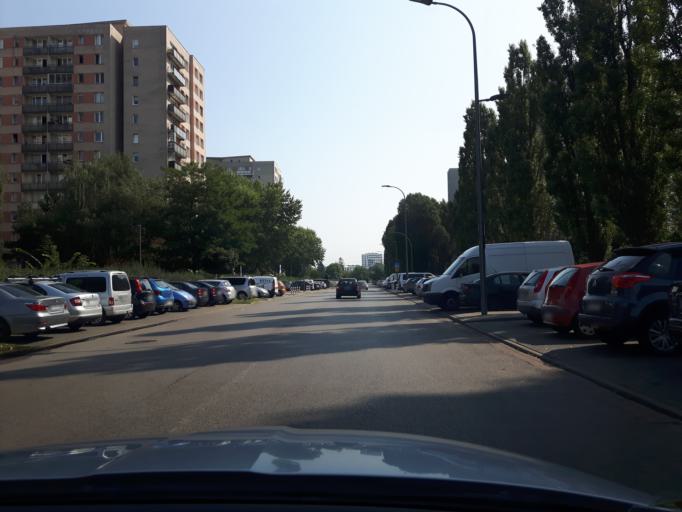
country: PL
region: Masovian Voivodeship
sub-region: Warszawa
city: Targowek
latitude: 52.2997
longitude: 21.0444
